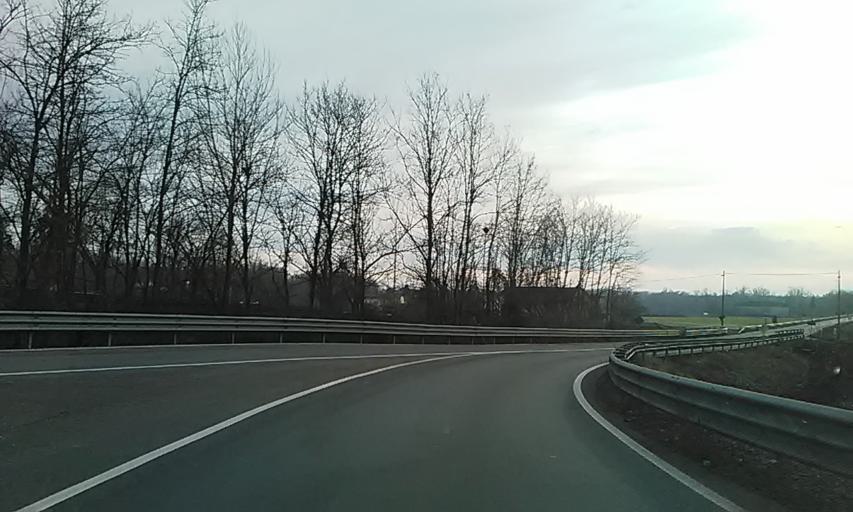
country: IT
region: Piedmont
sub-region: Provincia di Torino
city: Rondissone
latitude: 45.2704
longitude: 7.9799
